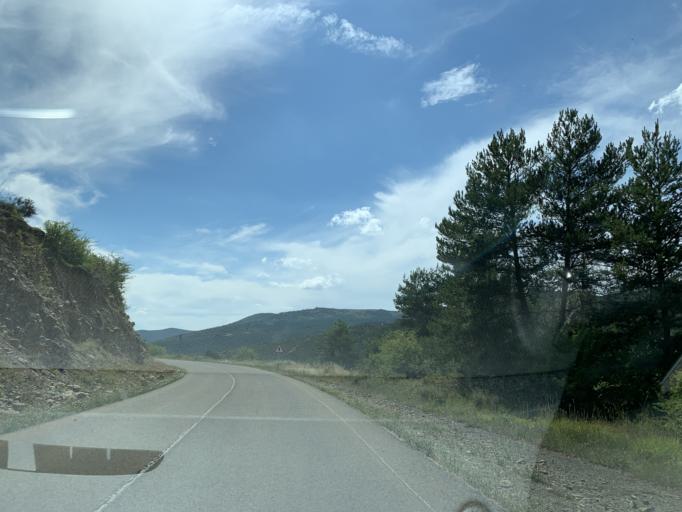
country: ES
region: Aragon
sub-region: Provincia de Huesca
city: Borau
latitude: 42.6623
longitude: -0.6281
